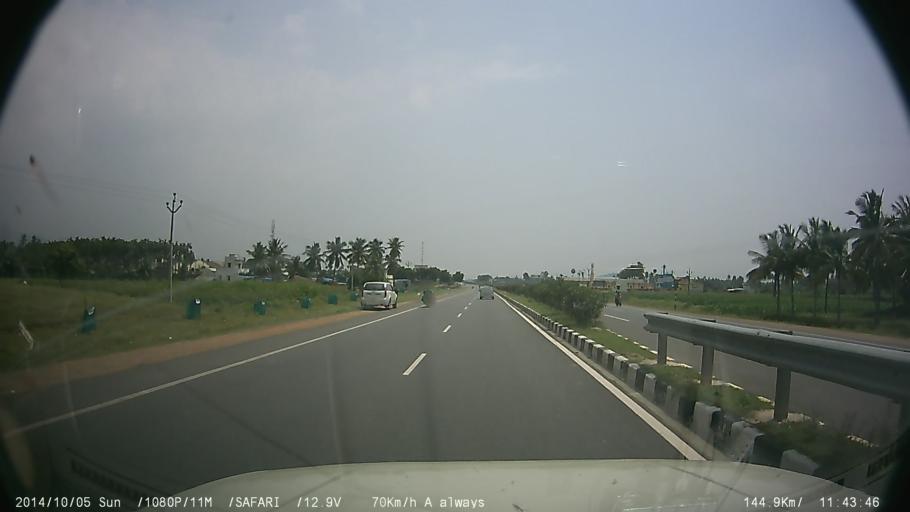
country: IN
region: Tamil Nadu
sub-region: Salem
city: Attur
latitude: 11.5923
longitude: 78.6252
